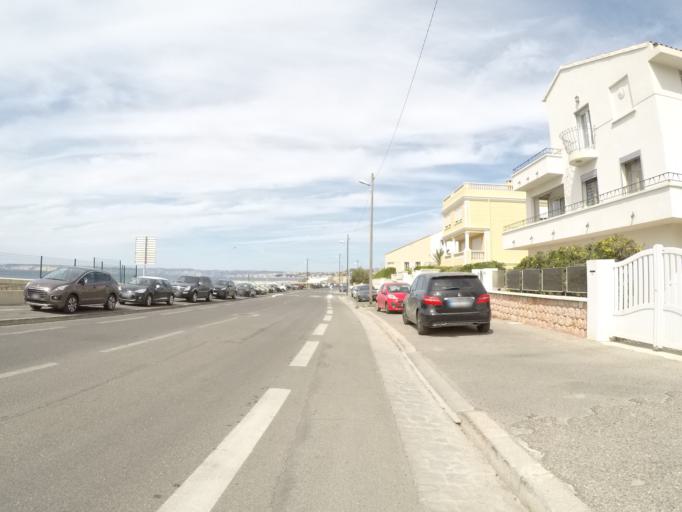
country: FR
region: Provence-Alpes-Cote d'Azur
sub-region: Departement des Bouches-du-Rhone
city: Marseille 08
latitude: 43.2397
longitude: 5.3629
